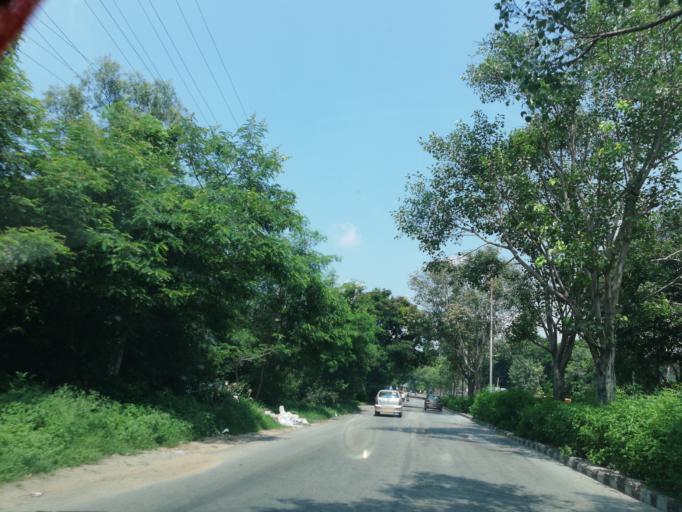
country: IN
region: Telangana
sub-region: Medak
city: Serilingampalle
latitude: 17.4606
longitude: 78.3370
